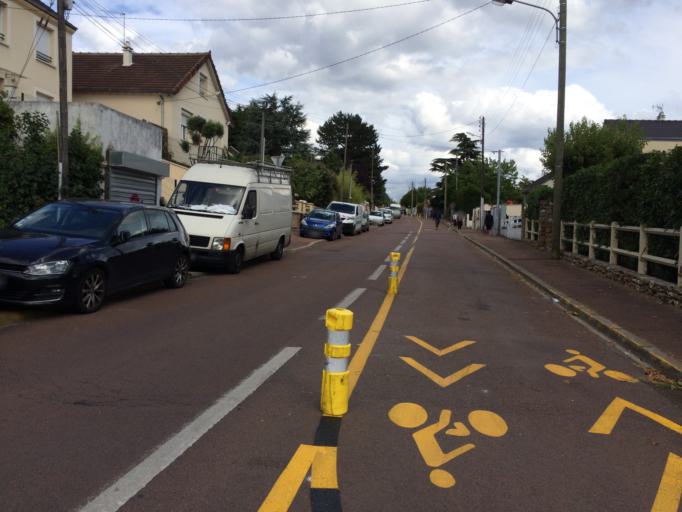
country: FR
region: Ile-de-France
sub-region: Departement de l'Essonne
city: Morangis
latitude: 48.6967
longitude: 2.3281
